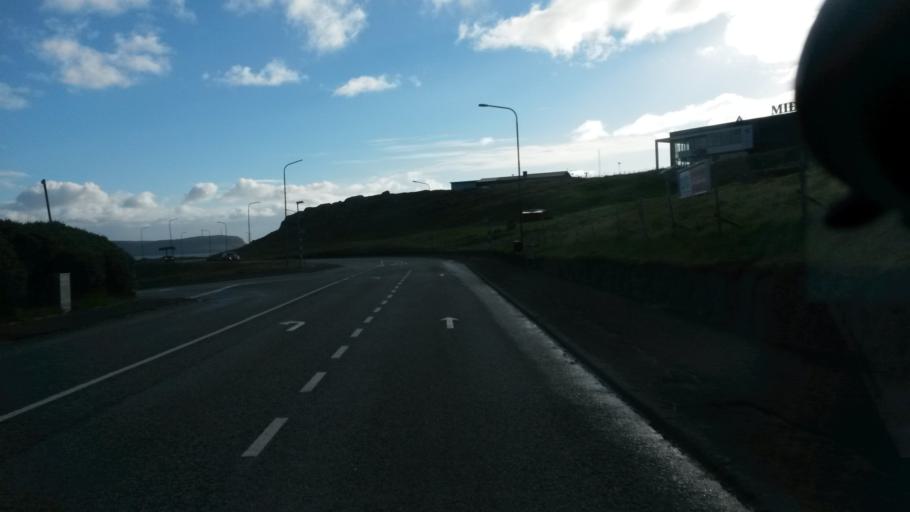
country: FO
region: Streymoy
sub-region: Torshavn
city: Torshavn
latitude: 62.0224
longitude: -6.7685
